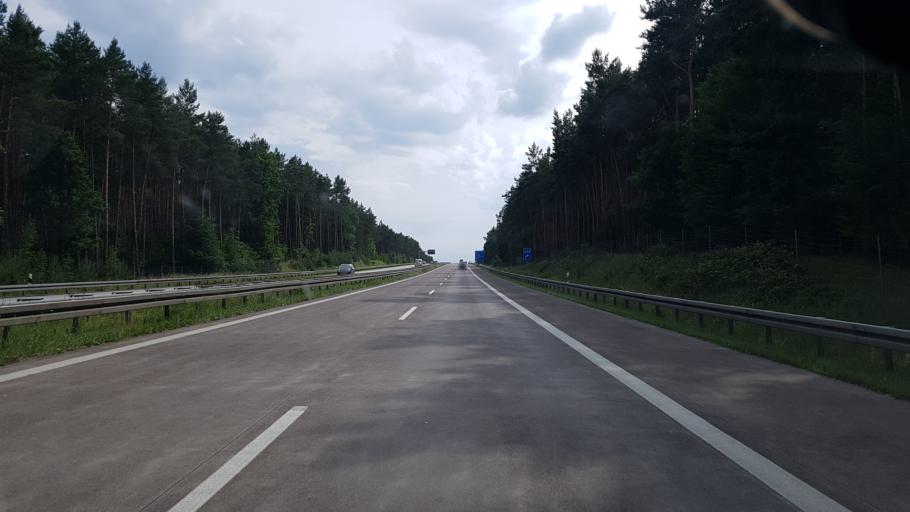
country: DE
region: Brandenburg
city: Althuttendorf
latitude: 52.9470
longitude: 13.8015
